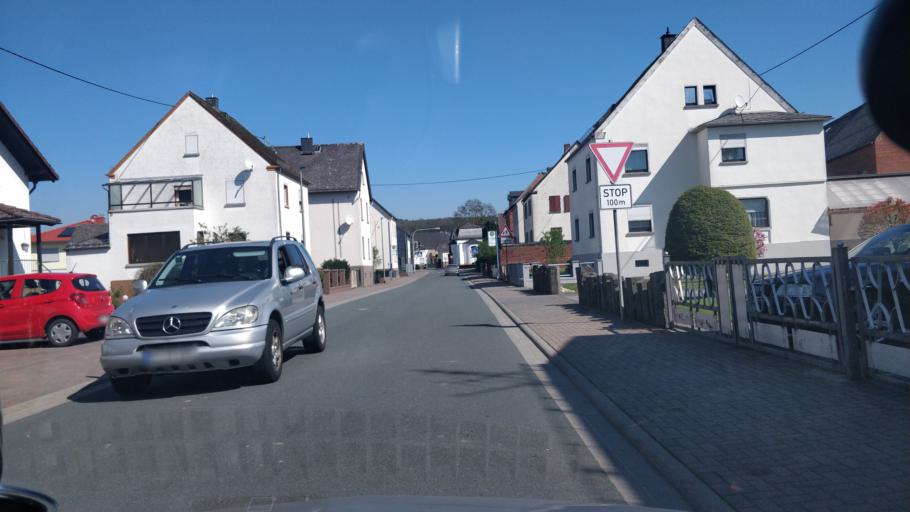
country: DE
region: Hesse
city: Waldbrunn
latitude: 50.4701
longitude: 8.1027
